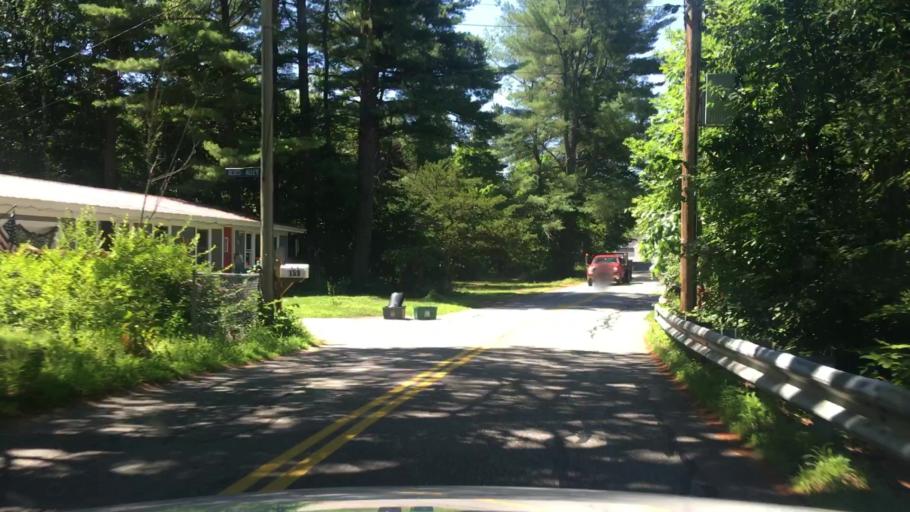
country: US
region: New Hampshire
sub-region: Merrimack County
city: Boscawen
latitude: 43.2502
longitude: -71.6186
